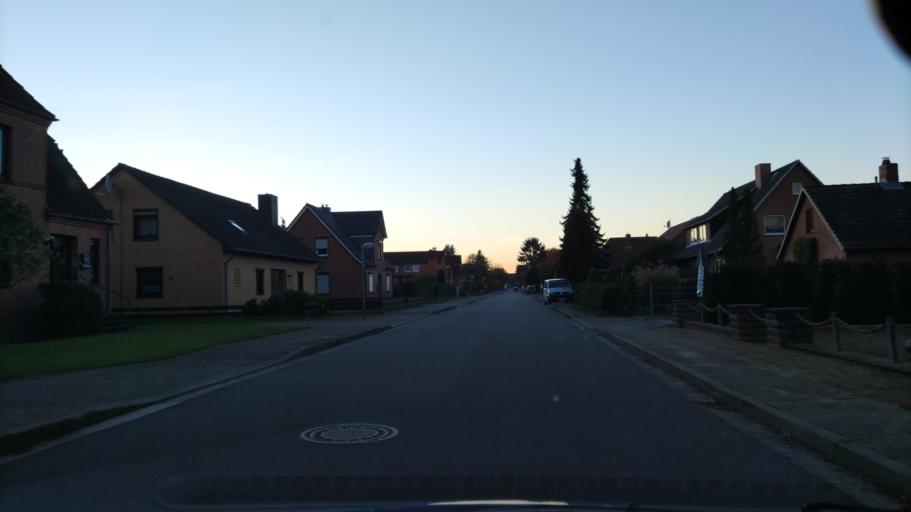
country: DE
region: Schleswig-Holstein
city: Lauenburg
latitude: 53.3655
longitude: 10.5571
